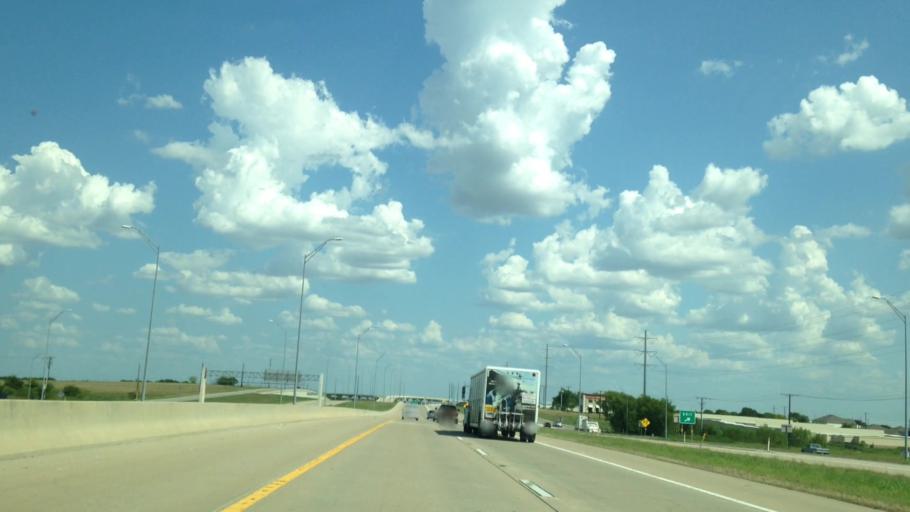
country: US
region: Texas
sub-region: Travis County
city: Pflugerville
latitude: 30.4809
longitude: -97.6078
